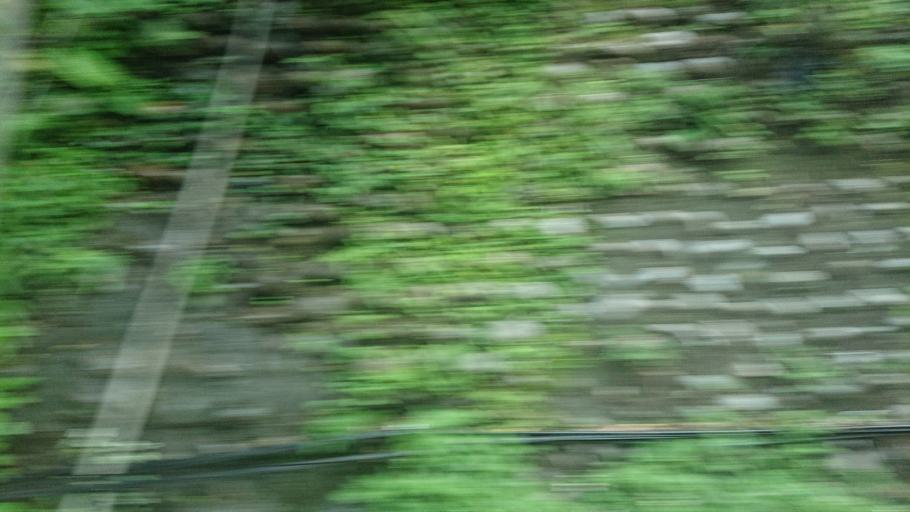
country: TW
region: Taiwan
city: Daxi
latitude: 24.8848
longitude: 121.3777
